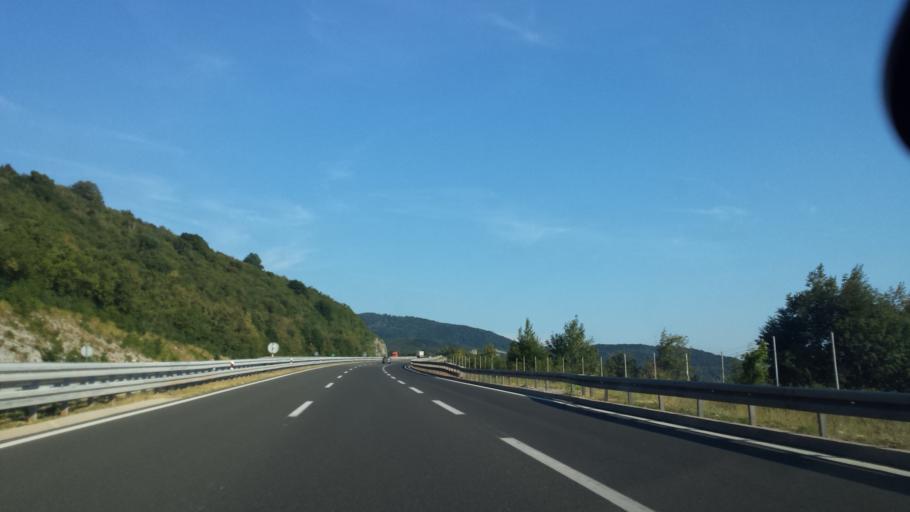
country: HR
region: Primorsko-Goranska
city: Krasica
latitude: 45.3554
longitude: 14.5797
